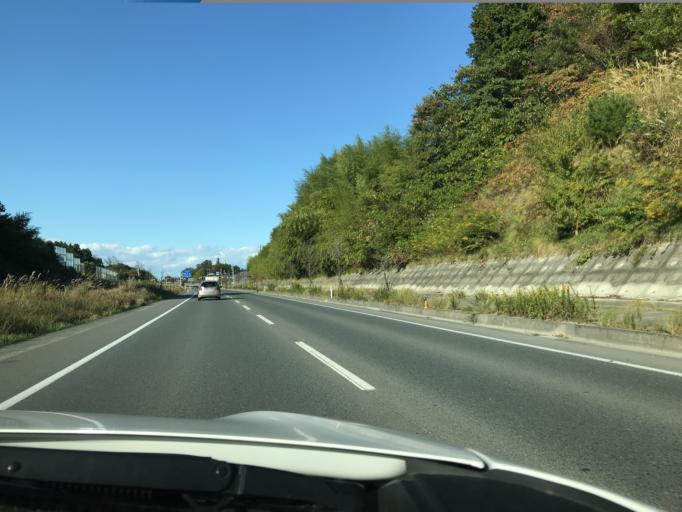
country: JP
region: Miyagi
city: Marumori
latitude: 37.8153
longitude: 140.9431
